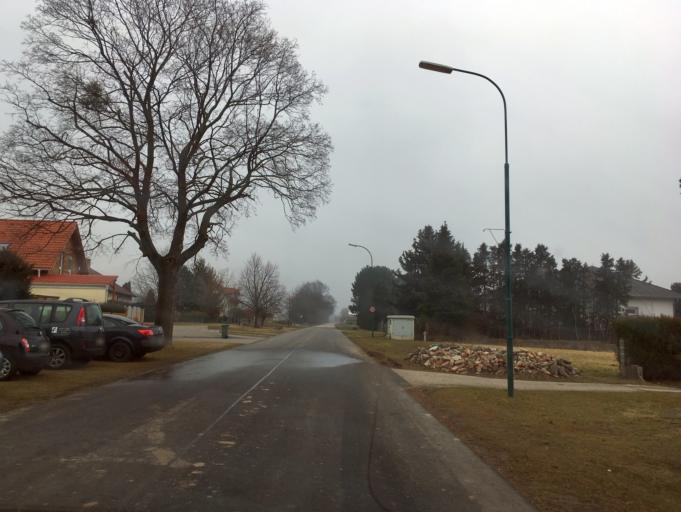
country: AT
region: Lower Austria
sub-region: Politischer Bezirk Bruck an der Leitha
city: Trautmannsdorf an der Leitha
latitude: 48.0399
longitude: 16.6770
